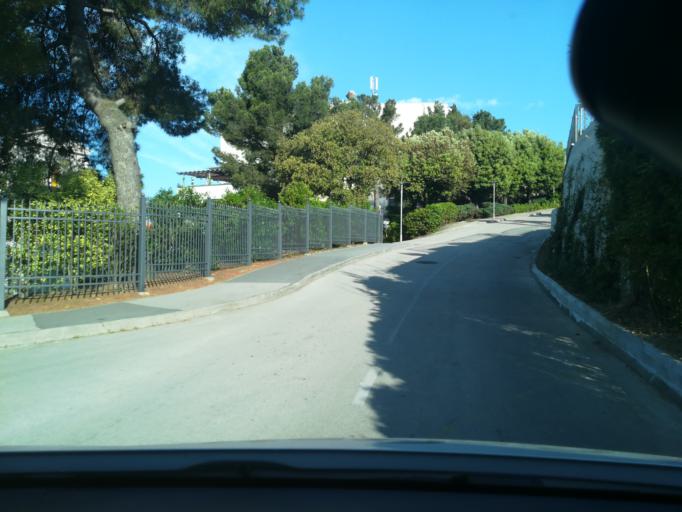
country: SI
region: Piran-Pirano
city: Piran
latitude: 45.5164
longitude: 13.5710
